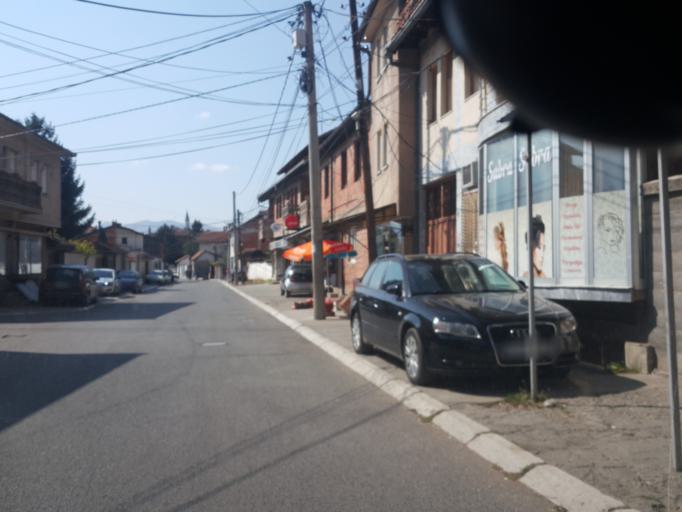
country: XK
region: Gjakova
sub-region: Komuna e Gjakoves
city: Gjakove
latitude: 42.3811
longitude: 20.4354
